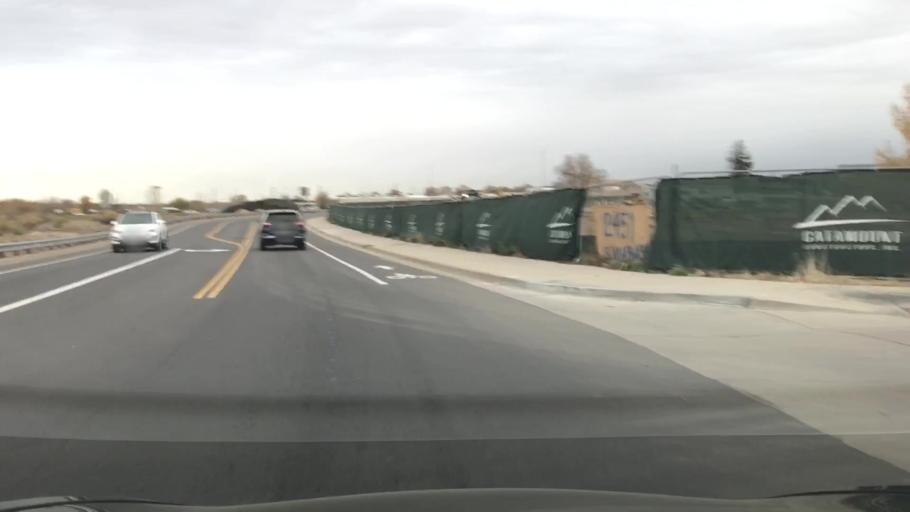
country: US
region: Colorado
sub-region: Arapahoe County
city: Glendale
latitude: 39.6711
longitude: -104.8897
